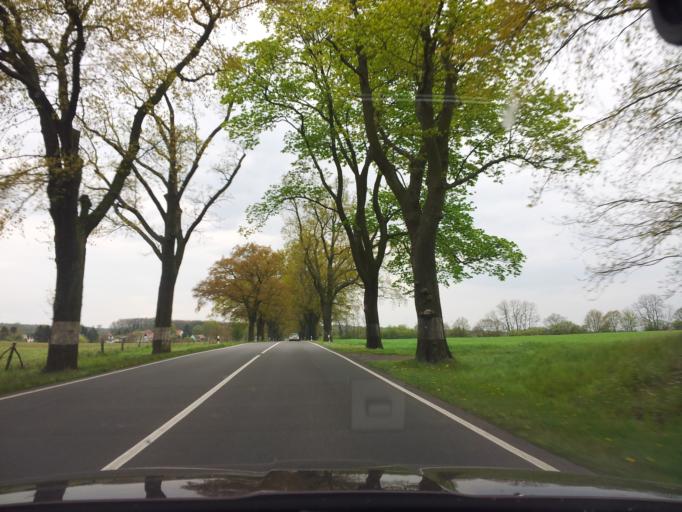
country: DE
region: Brandenburg
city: Neuhardenberg
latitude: 52.5092
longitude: 14.2470
